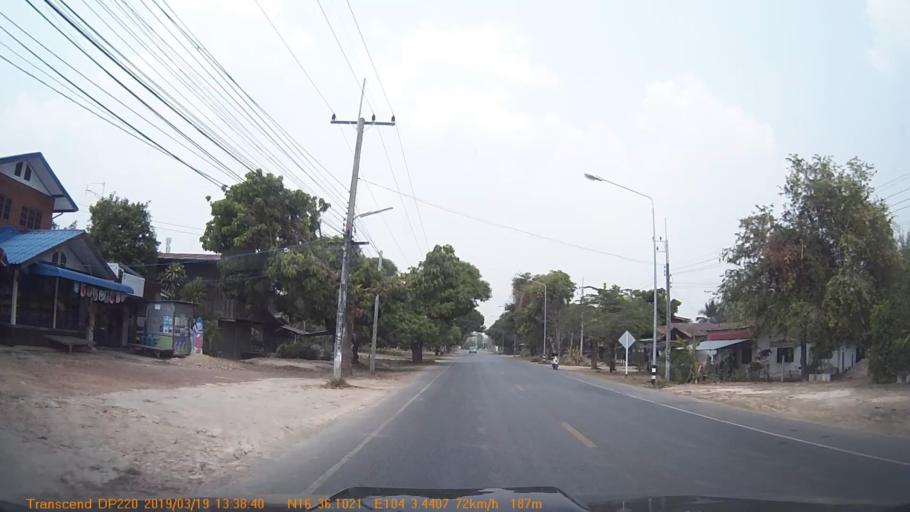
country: TH
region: Kalasin
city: Kuchinarai
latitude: 16.6021
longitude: 104.0575
